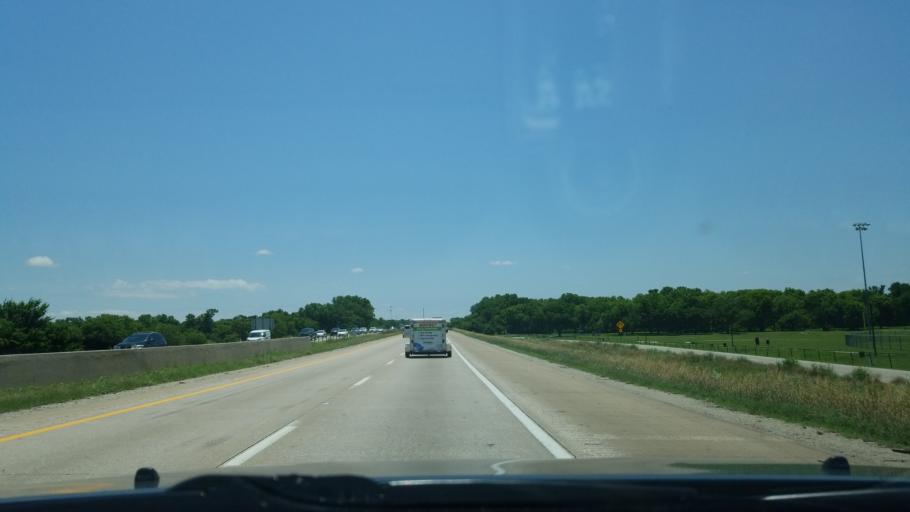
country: US
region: Texas
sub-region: Denton County
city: Sanger
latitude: 33.3422
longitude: -97.1818
